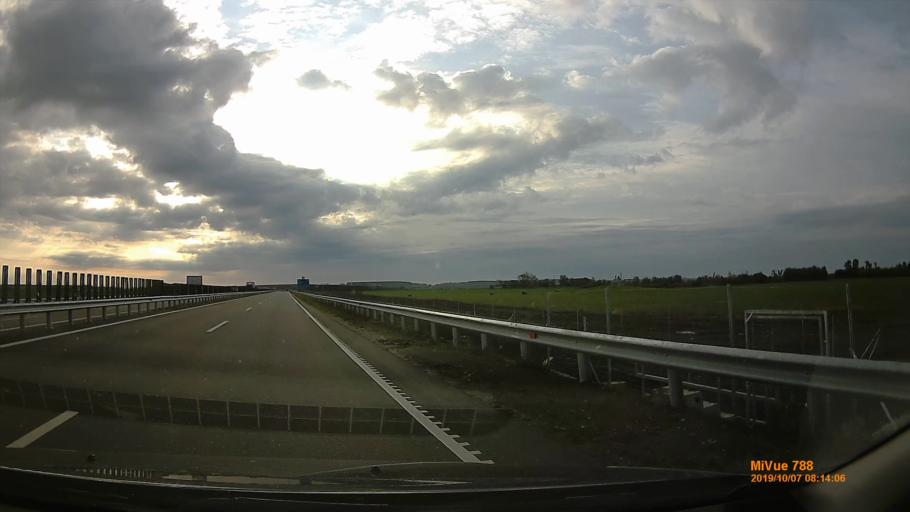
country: HU
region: Jasz-Nagykun-Szolnok
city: Kunszentmarton
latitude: 46.8761
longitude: 20.2548
